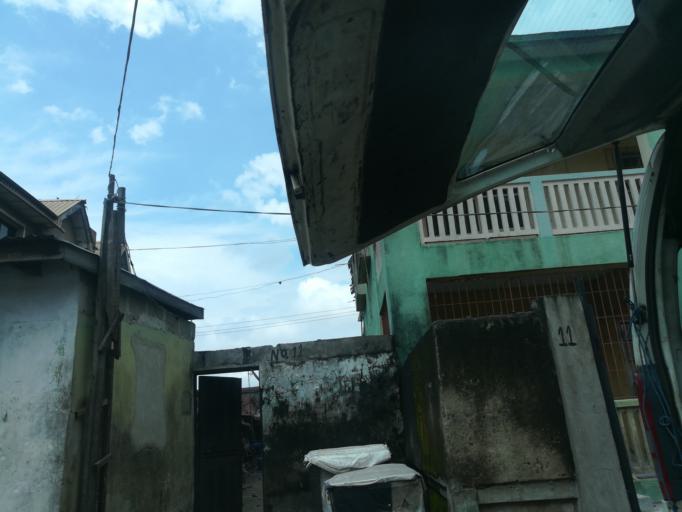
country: NG
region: Lagos
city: Mushin
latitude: 6.5205
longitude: 3.3668
